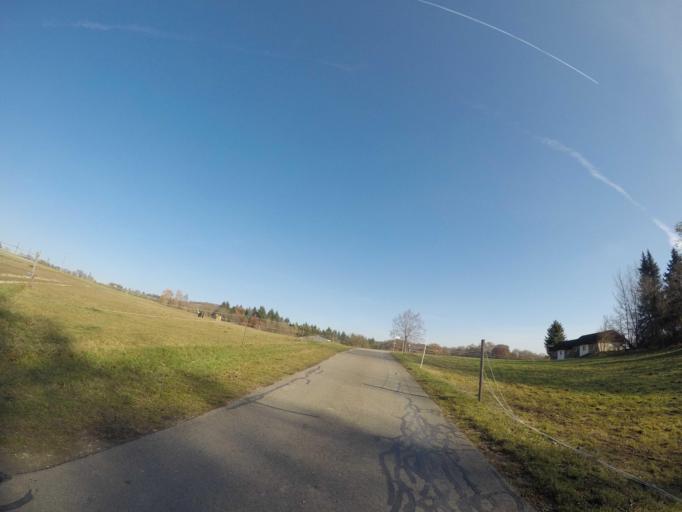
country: DE
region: Baden-Wuerttemberg
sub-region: Tuebingen Region
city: Rechtenstein
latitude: 48.2430
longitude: 9.5518
